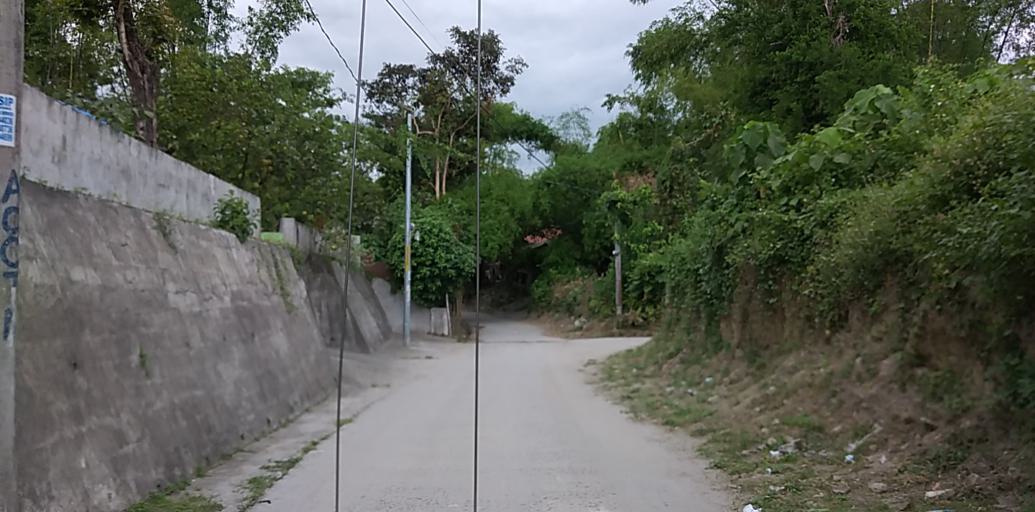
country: PH
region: Central Luzon
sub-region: Province of Pampanga
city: Pulung Santol
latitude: 15.0438
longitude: 120.5629
